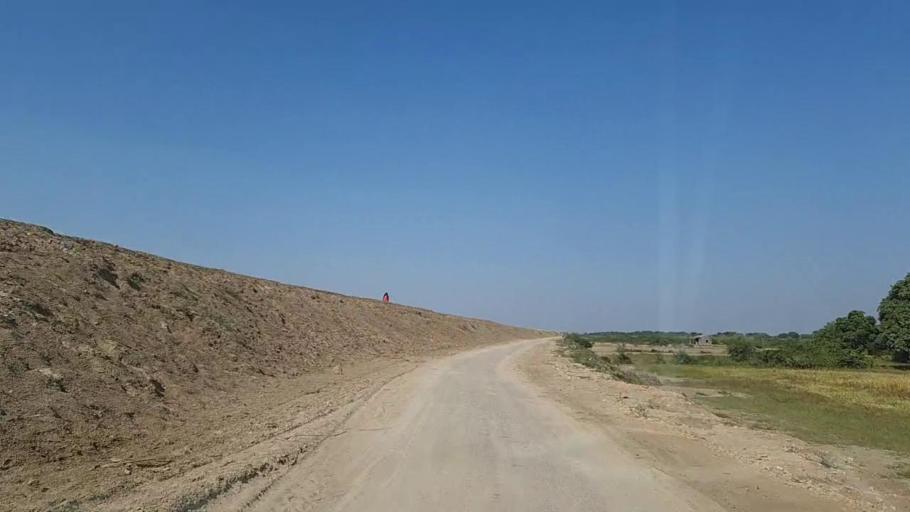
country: PK
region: Sindh
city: Chuhar Jamali
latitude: 24.5601
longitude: 68.0280
